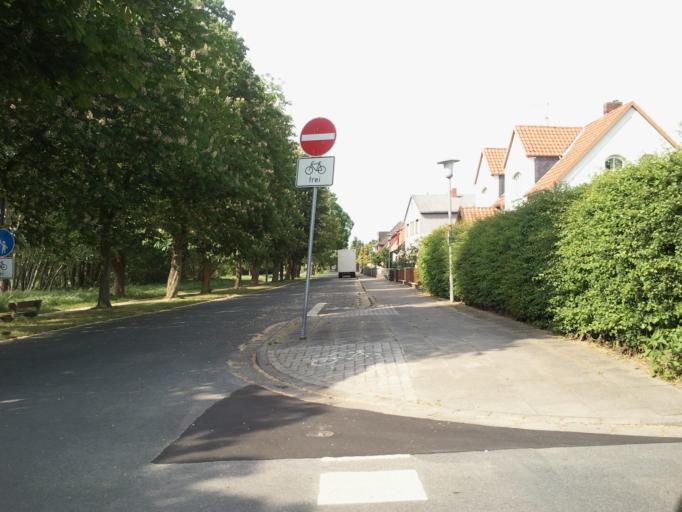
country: DE
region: Lower Saxony
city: Nienburg
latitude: 52.6268
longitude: 9.2092
